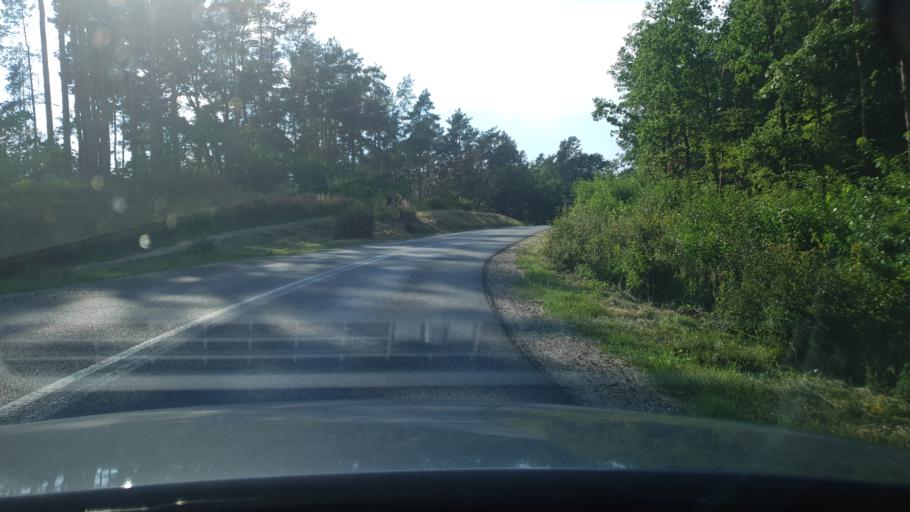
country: PL
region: Kujawsko-Pomorskie
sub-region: Grudziadz
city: Grudziadz
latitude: 53.4454
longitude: 18.7458
